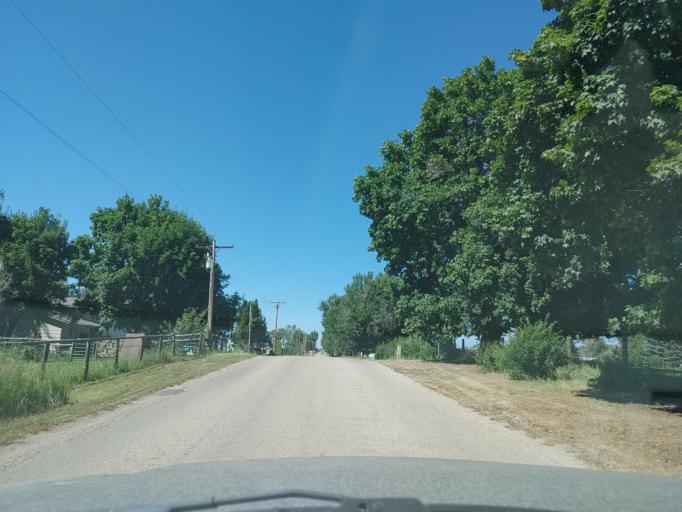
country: US
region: Montana
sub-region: Ravalli County
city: Hamilton
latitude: 46.3255
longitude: -114.0613
